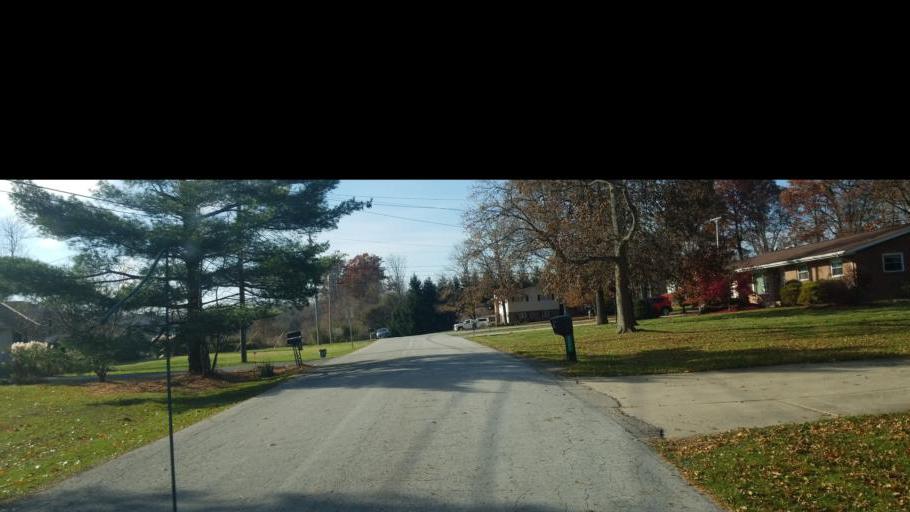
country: US
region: Ohio
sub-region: Richland County
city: Lexington
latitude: 40.7106
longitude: -82.5583
